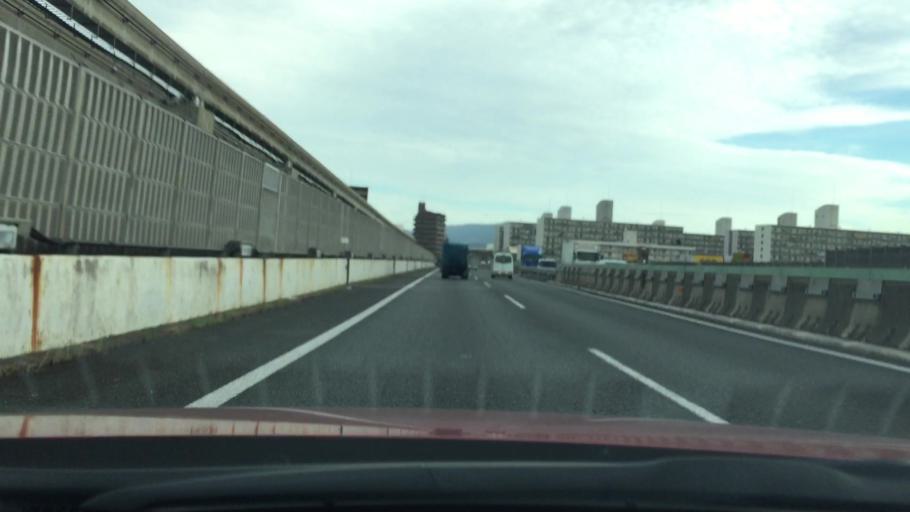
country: JP
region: Osaka
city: Ibaraki
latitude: 34.7957
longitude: 135.5661
